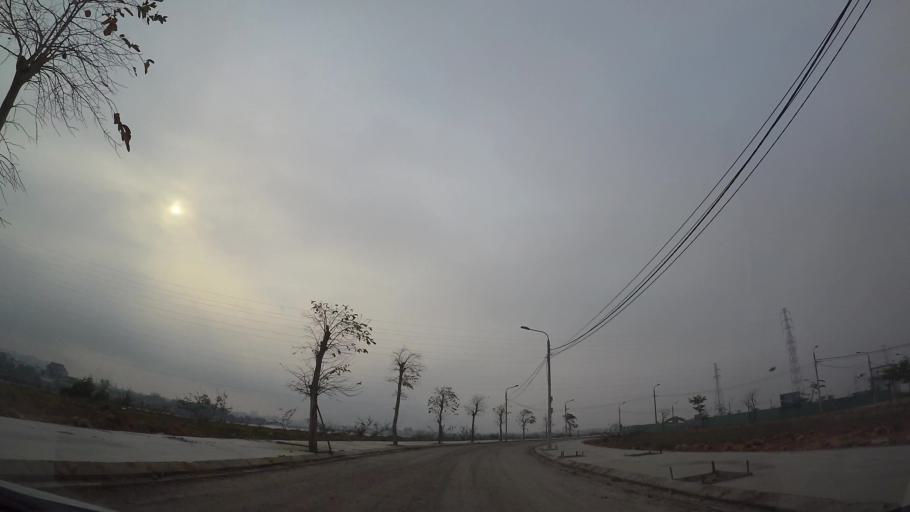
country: VN
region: Da Nang
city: Ngu Hanh Son
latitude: 16.0227
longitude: 108.2375
